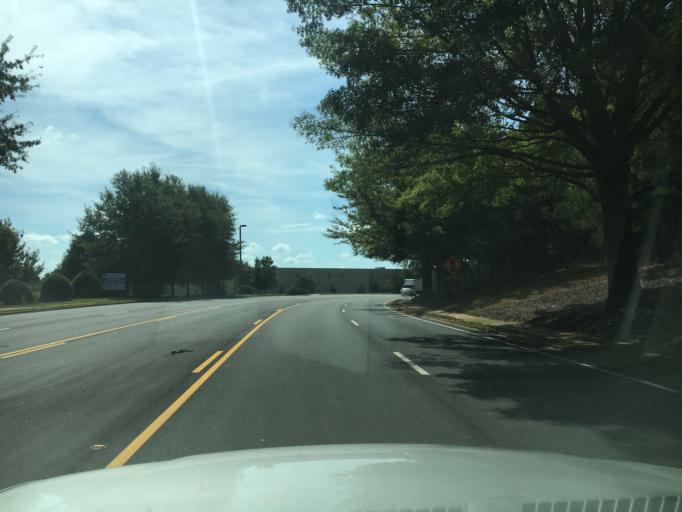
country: US
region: Georgia
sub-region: Gwinnett County
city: Duluth
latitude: 33.9744
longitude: -84.1114
